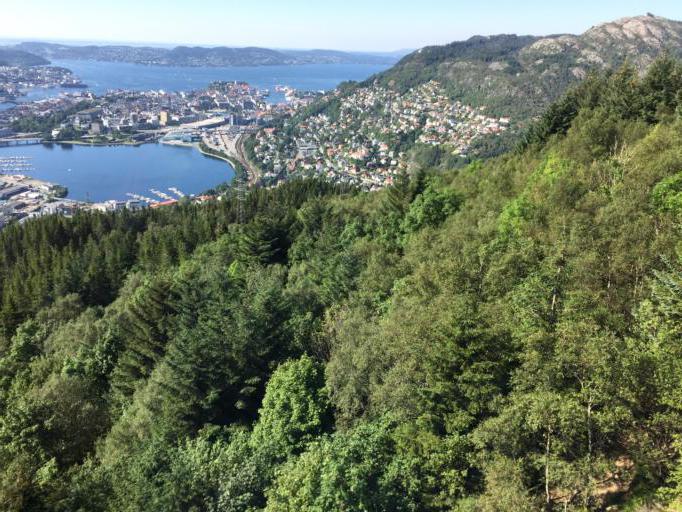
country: NO
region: Hordaland
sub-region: Bergen
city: Bergen
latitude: 60.3757
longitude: 5.3725
